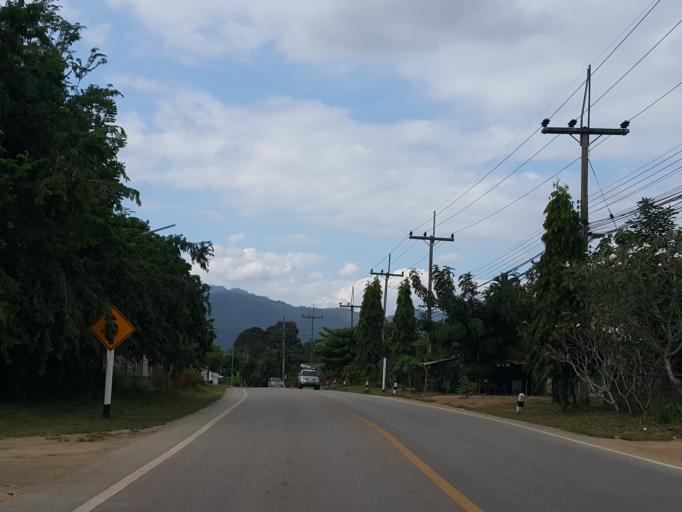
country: TH
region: Lampang
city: Chae Hom
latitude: 18.5711
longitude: 99.4712
